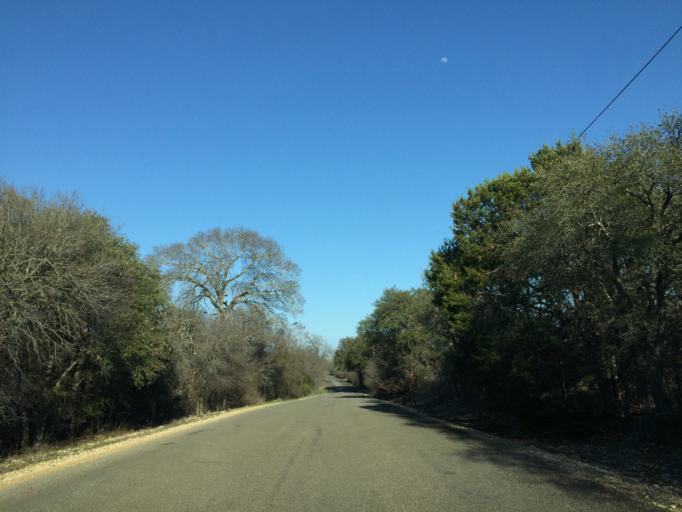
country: US
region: Texas
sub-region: Williamson County
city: Florence
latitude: 30.7774
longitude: -97.8021
